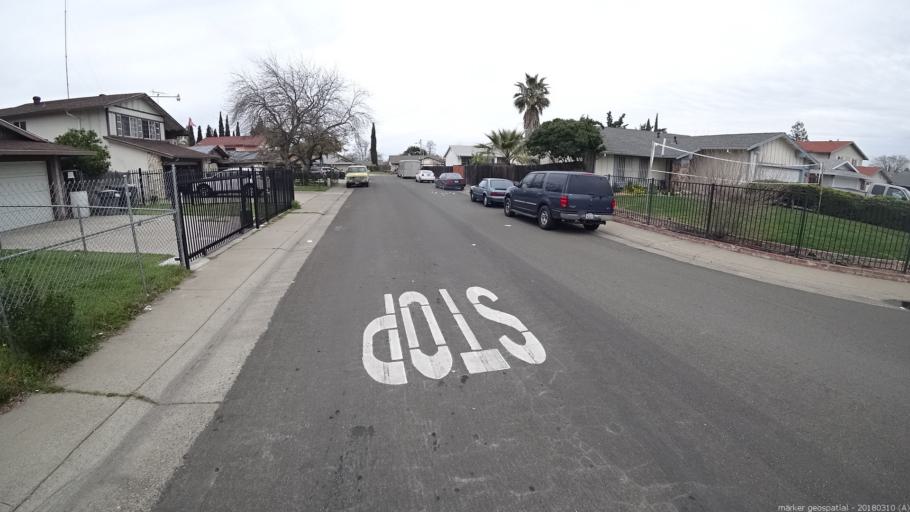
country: US
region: California
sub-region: Sacramento County
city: Florin
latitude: 38.4878
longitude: -121.4072
